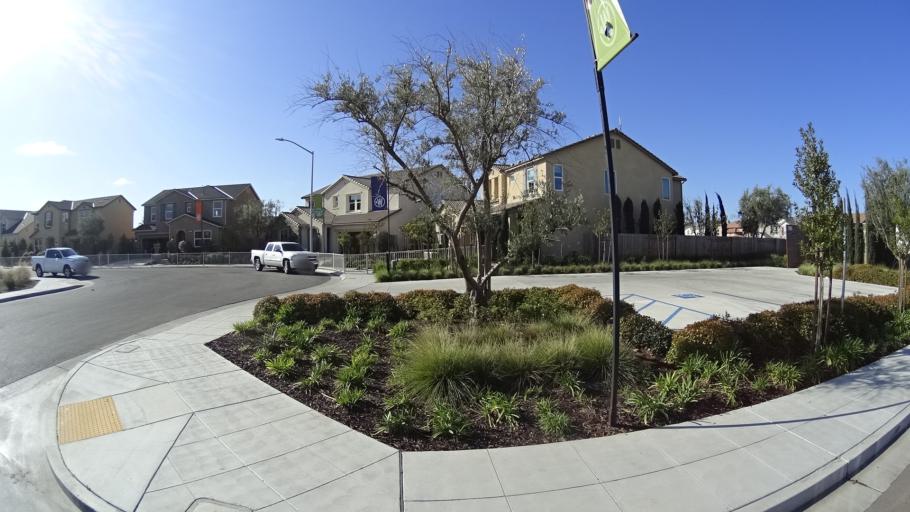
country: US
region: California
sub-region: Fresno County
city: West Park
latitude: 36.7994
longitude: -119.9062
